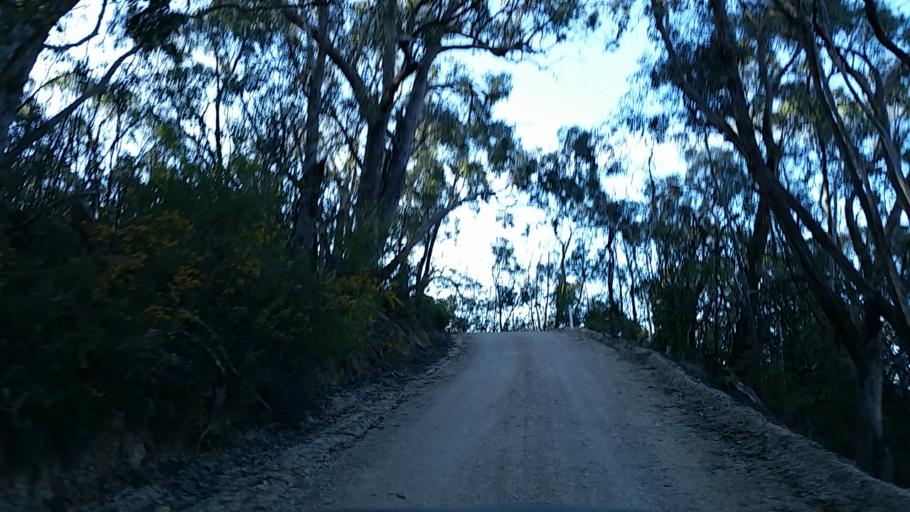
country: AU
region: South Australia
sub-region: Mount Barker
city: Meadows
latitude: -35.2347
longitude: 138.7501
